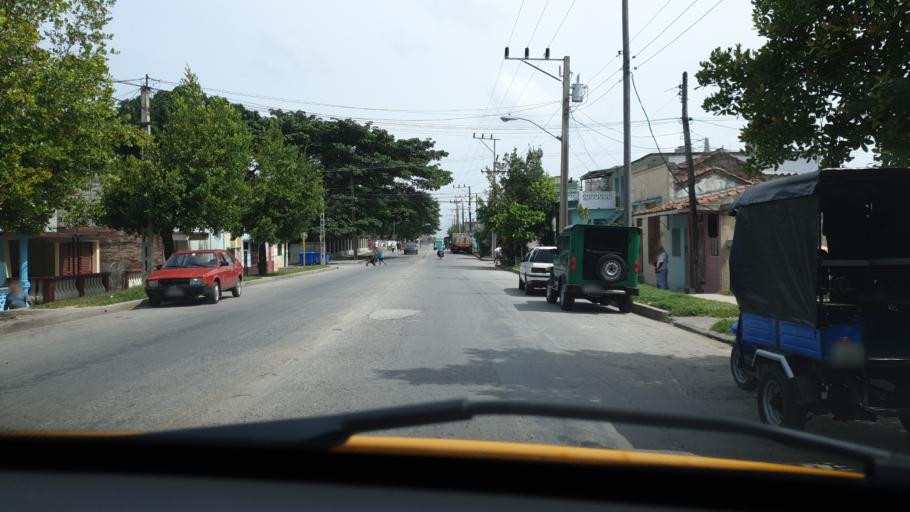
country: CU
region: Villa Clara
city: Santa Clara
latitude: 22.3931
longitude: -79.9613
